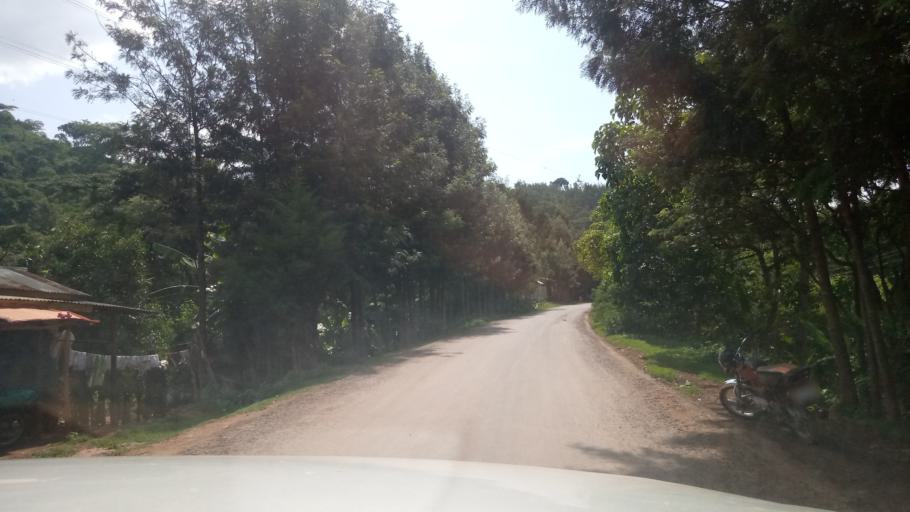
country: ET
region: Oromiya
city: Agaro
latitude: 7.9220
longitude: 36.5175
